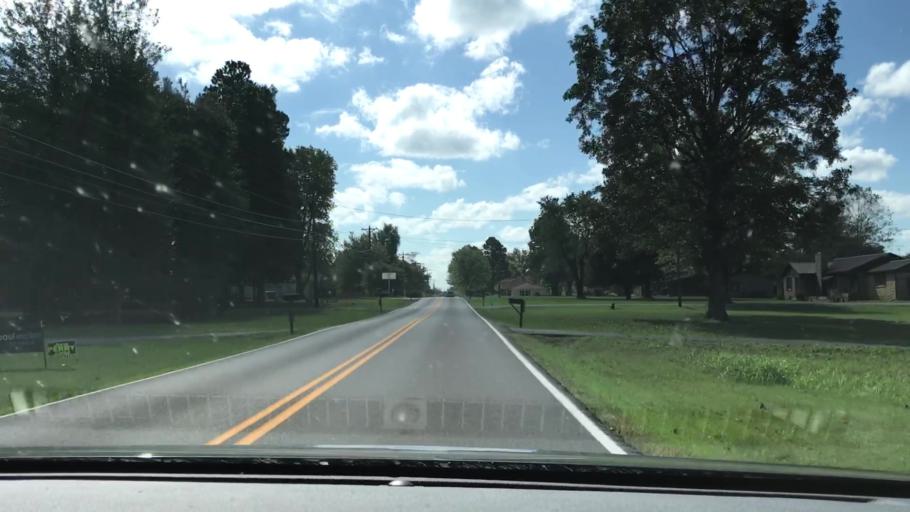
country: US
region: Kentucky
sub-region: McCracken County
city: Reidland
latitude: 36.9240
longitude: -88.5195
